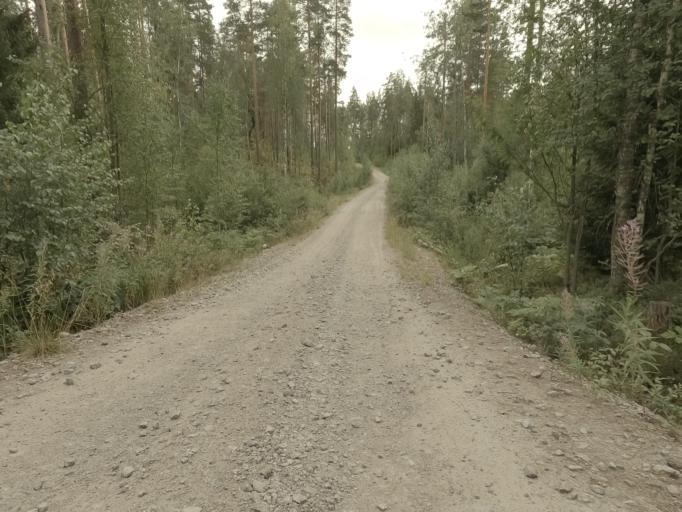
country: RU
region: Leningrad
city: Kamennogorsk
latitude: 60.9803
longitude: 29.1717
